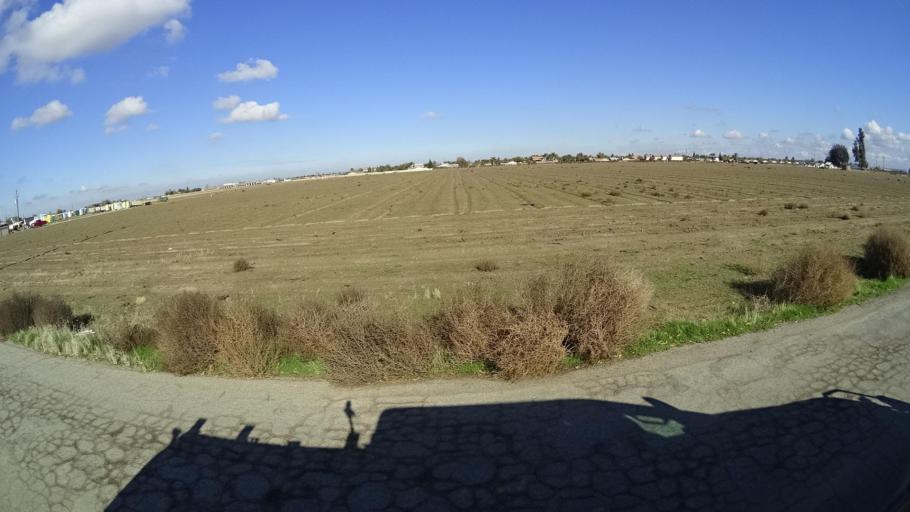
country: US
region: California
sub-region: Kern County
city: McFarland
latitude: 35.6599
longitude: -119.2354
